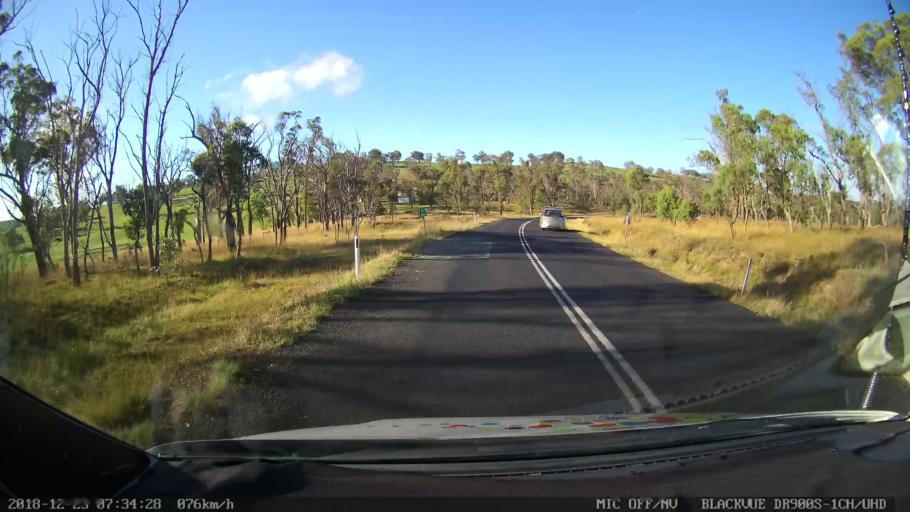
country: AU
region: New South Wales
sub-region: Armidale Dumaresq
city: Enmore
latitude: -30.5202
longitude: 152.0932
